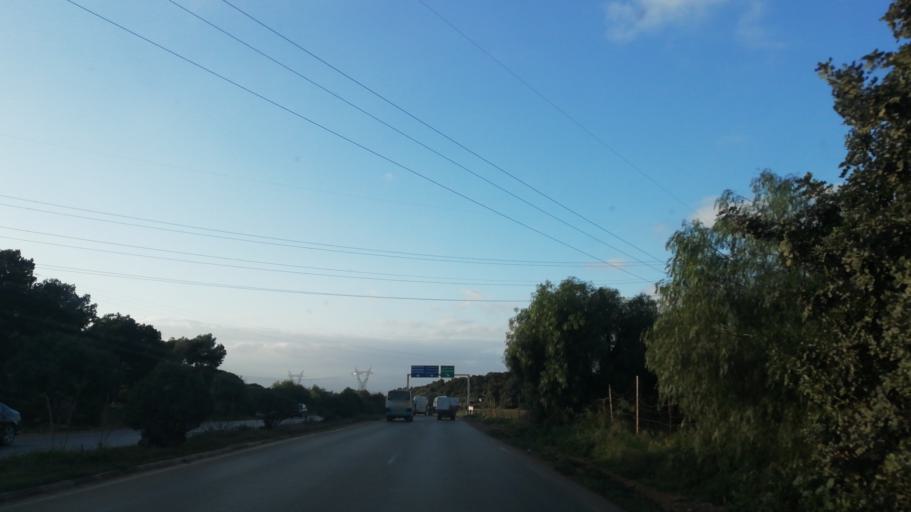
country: DZ
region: Oran
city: Oran
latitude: 35.6385
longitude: -0.7106
